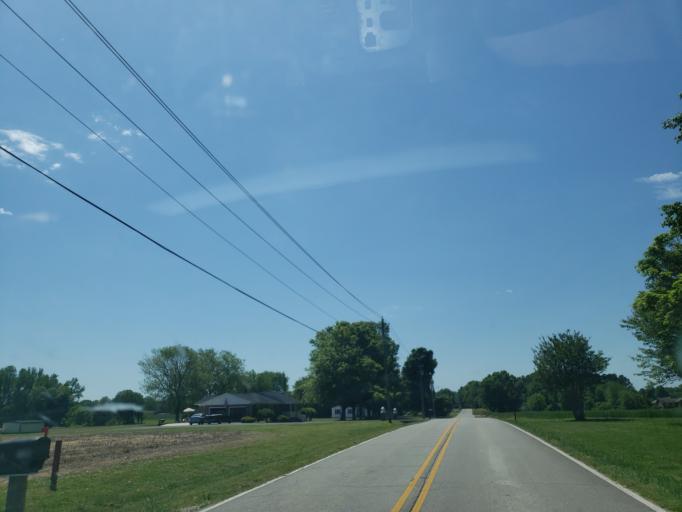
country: US
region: Alabama
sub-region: Madison County
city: Hazel Green
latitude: 34.9634
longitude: -86.5402
